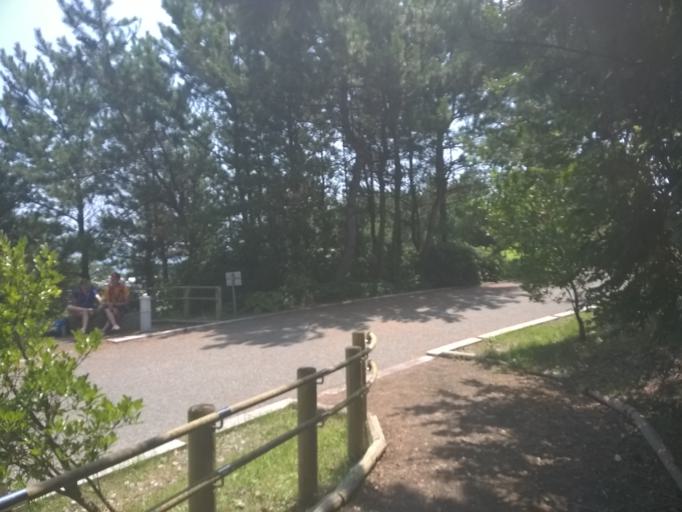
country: JP
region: Yamaguchi
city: Ogori-shimogo
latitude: 34.0072
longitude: 131.3739
